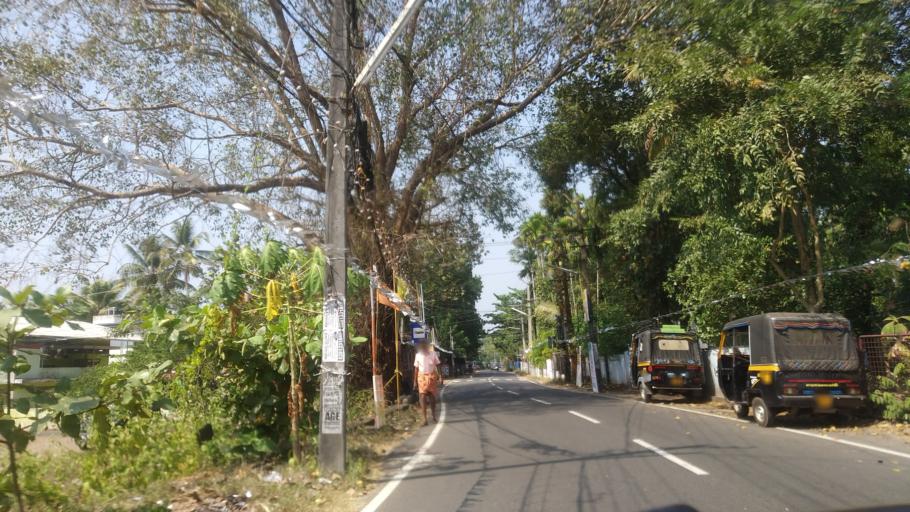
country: IN
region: Kerala
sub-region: Ernakulam
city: Elur
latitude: 10.1258
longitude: 76.2376
